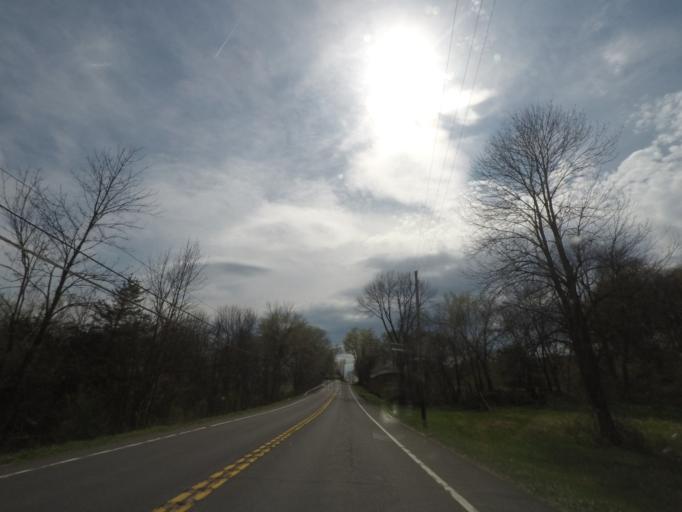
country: US
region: New York
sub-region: Columbia County
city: Stottville
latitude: 42.2871
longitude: -73.6995
